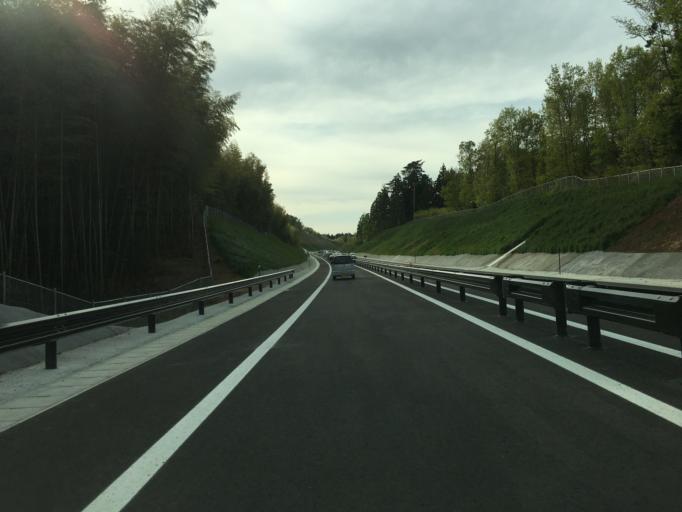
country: JP
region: Fukushima
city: Hobaramachi
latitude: 37.7891
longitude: 140.5590
